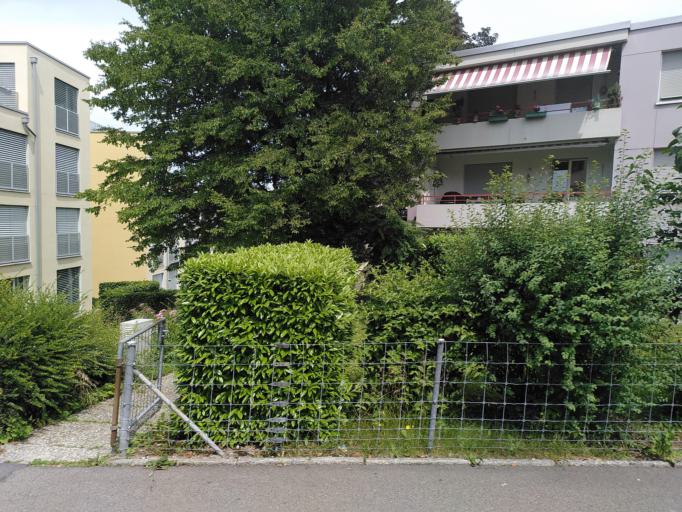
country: CH
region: Zurich
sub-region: Bezirk Horgen
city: Thalwil
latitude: 47.2930
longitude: 8.5623
